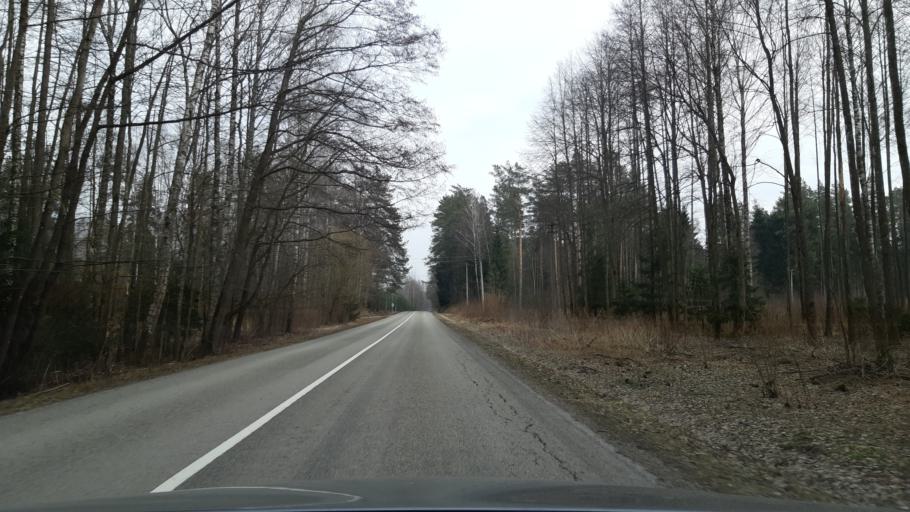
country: LT
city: Kazlu Ruda
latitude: 54.7374
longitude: 23.3744
